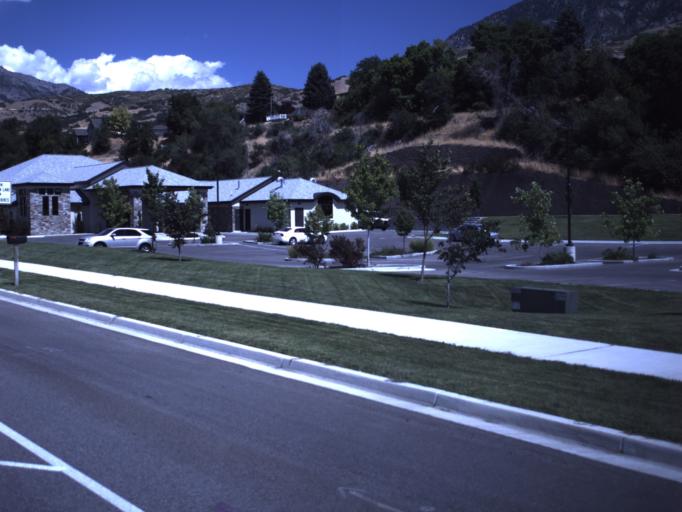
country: US
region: Utah
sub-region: Utah County
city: Orem
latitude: 40.2964
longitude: -111.6572
